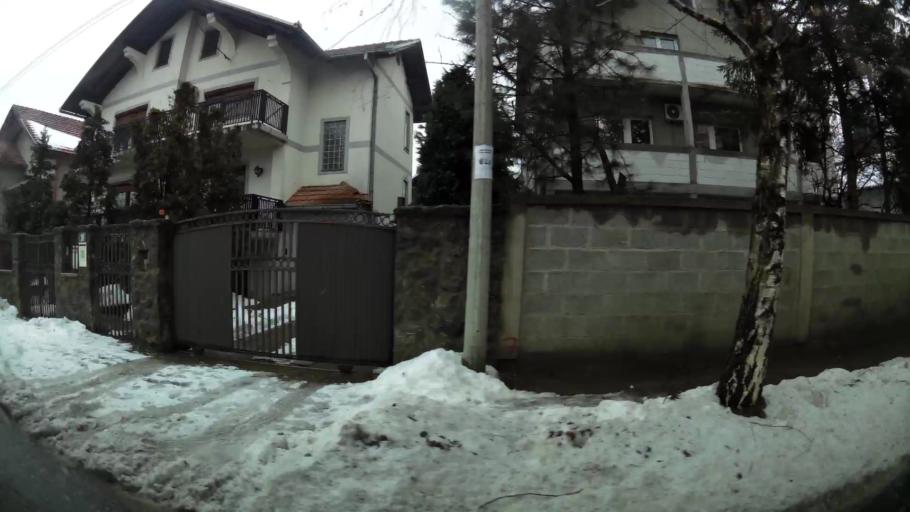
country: RS
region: Central Serbia
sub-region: Belgrade
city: Zemun
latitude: 44.8507
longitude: 20.3573
